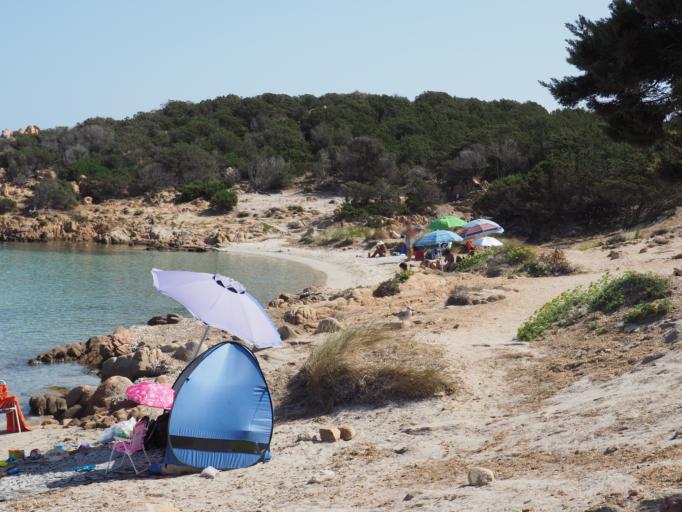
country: IT
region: Sardinia
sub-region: Provincia di Olbia-Tempio
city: Porto Cervo
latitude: 41.1769
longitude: 9.4706
